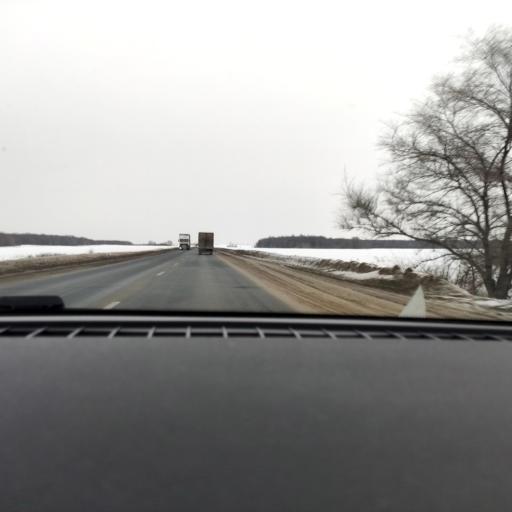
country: RU
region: Samara
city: Petra-Dubrava
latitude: 53.3221
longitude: 50.4550
